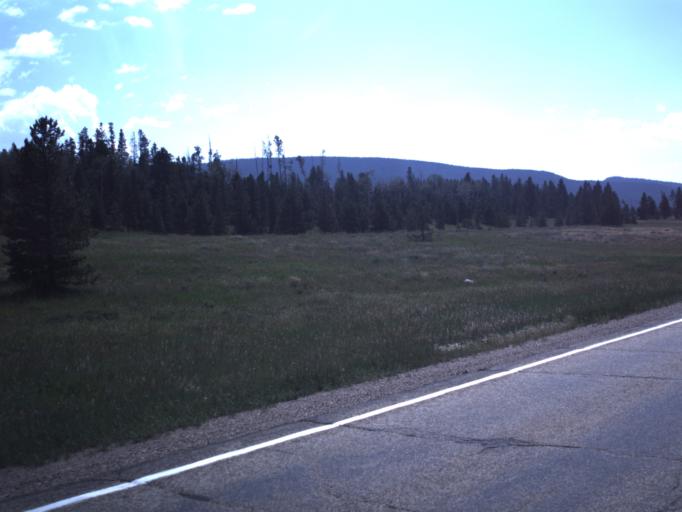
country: US
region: Utah
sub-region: Daggett County
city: Manila
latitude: 40.8033
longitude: -109.4670
